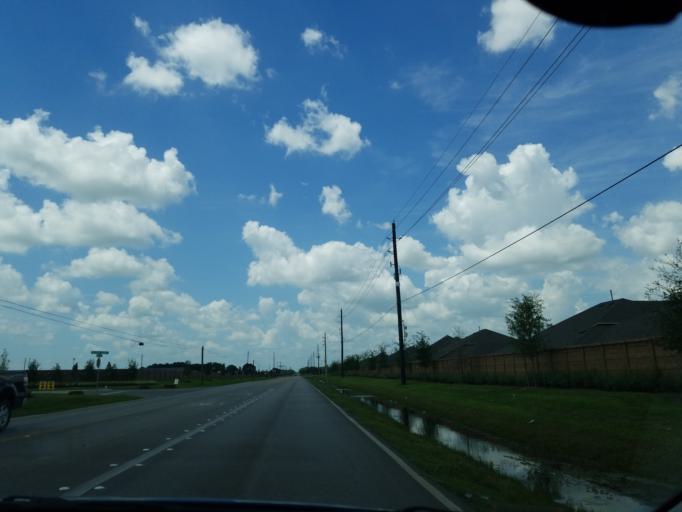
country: US
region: Texas
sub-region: Harris County
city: Katy
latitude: 29.8476
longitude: -95.8069
